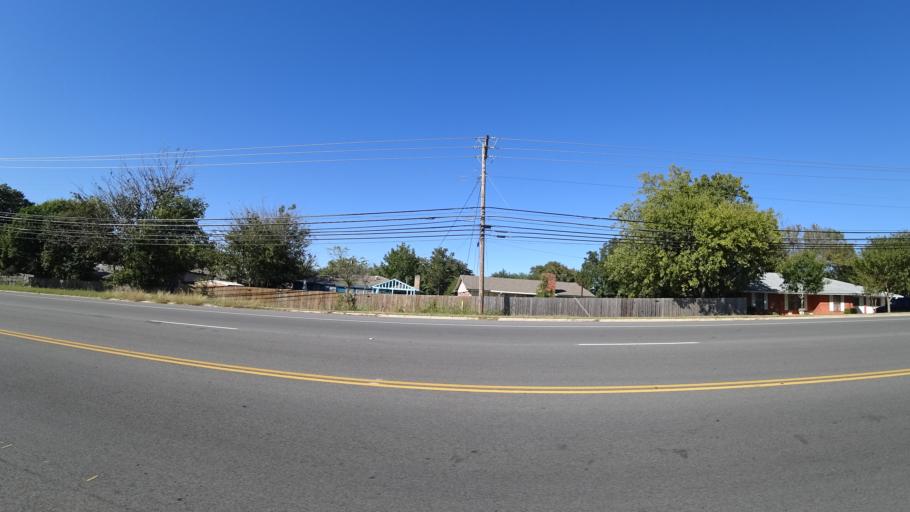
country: US
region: Texas
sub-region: Travis County
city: Austin
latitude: 30.2867
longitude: -97.6726
